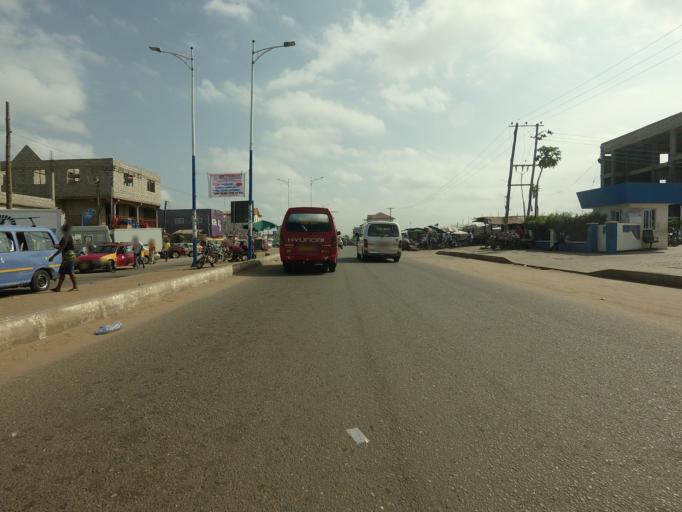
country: GH
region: Greater Accra
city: Tema
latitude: 5.6896
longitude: -0.0277
